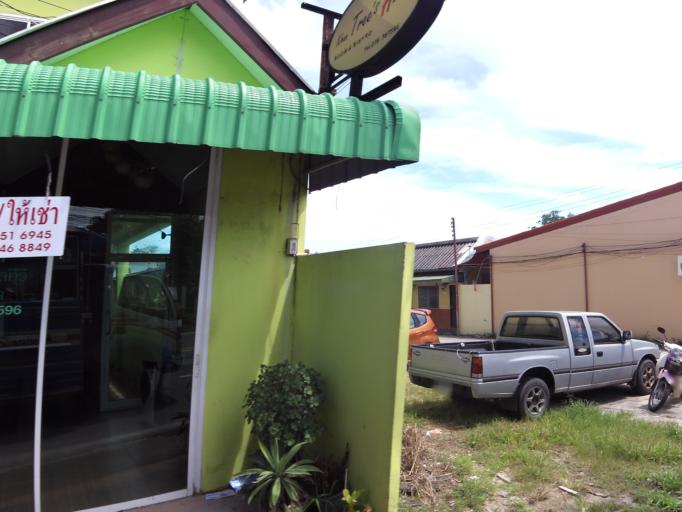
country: TH
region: Phuket
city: Ban Chalong
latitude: 7.8521
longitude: 98.3361
